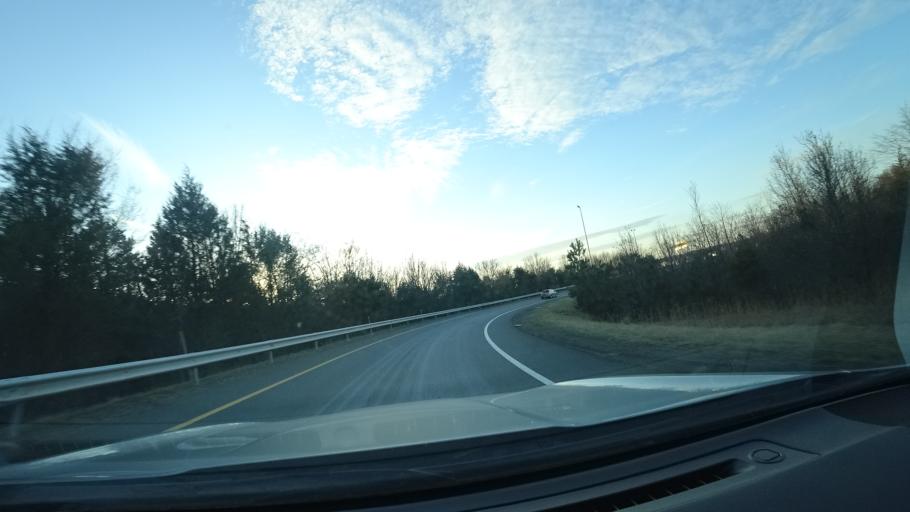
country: US
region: Virginia
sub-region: Fairfax County
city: Floris
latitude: 38.9606
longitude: -77.4259
